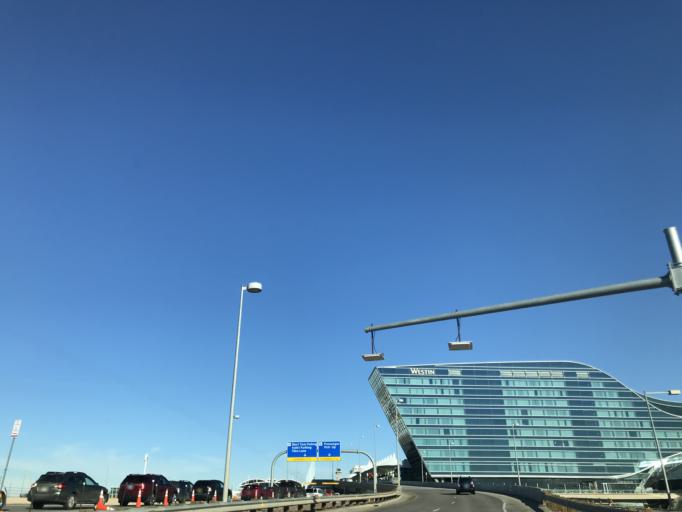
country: US
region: Colorado
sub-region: Weld County
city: Lochbuie
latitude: 39.8460
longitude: -104.6753
